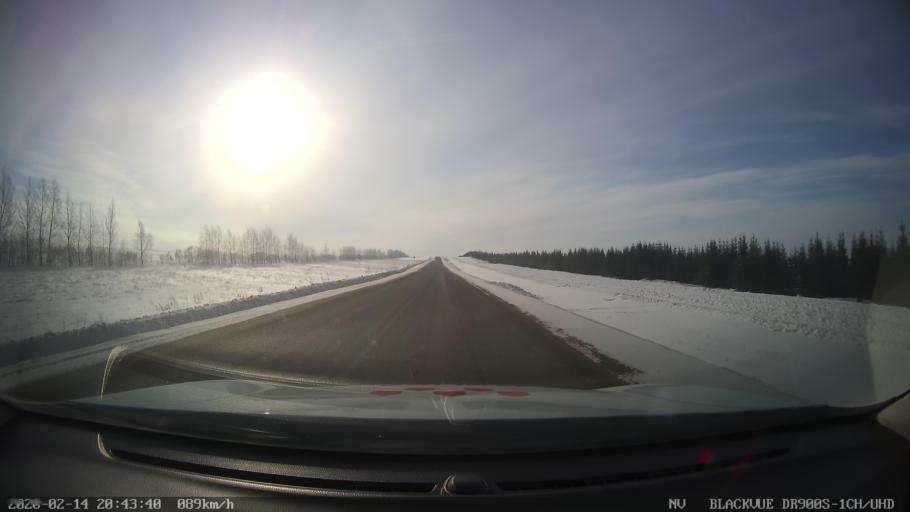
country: RU
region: Tatarstan
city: Kuybyshevskiy Zaton
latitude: 55.3050
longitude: 49.1482
